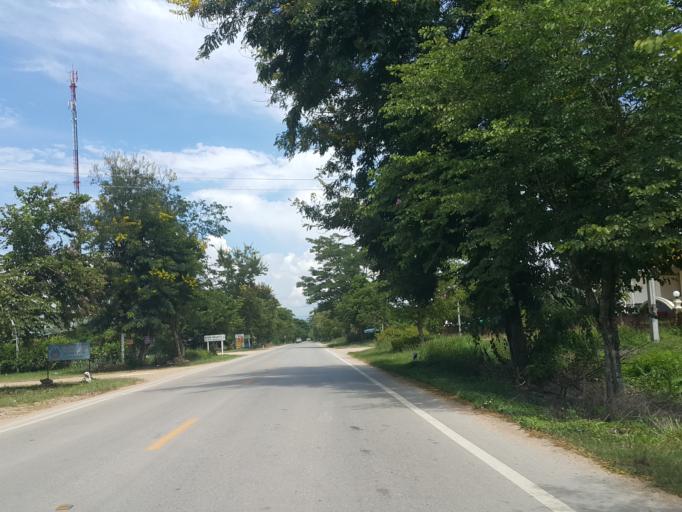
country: TH
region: Chiang Mai
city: Phrao
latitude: 19.3093
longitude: 99.1899
